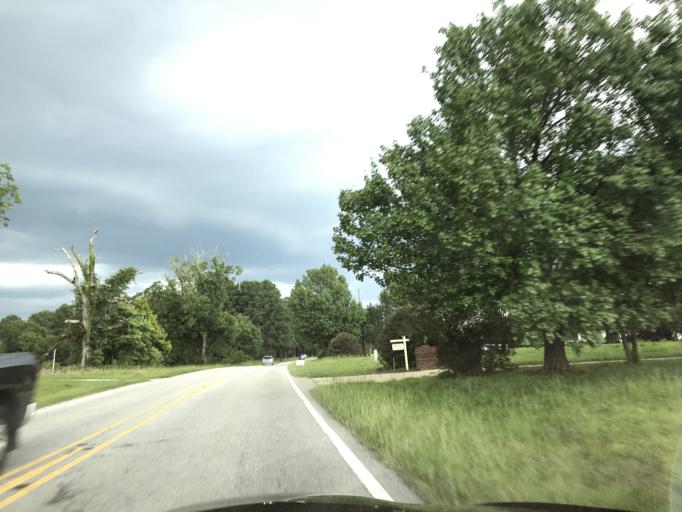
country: US
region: North Carolina
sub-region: Johnston County
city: Four Oaks
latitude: 35.5146
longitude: -78.5026
